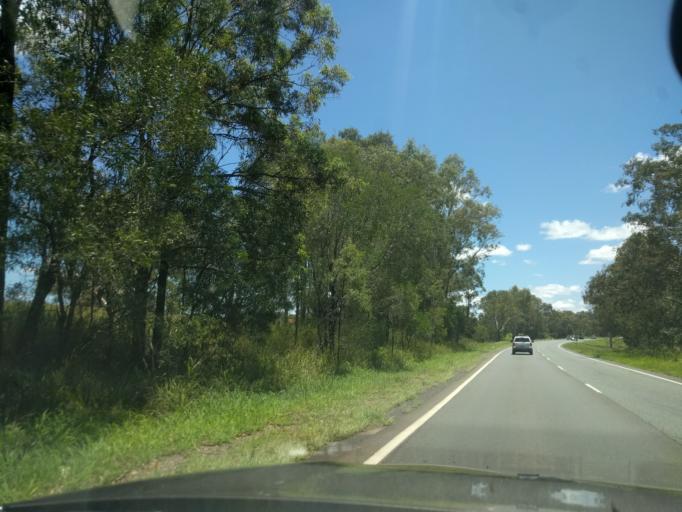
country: AU
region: Queensland
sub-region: Logan
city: Cedar Vale
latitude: -27.8605
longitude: 153.0023
